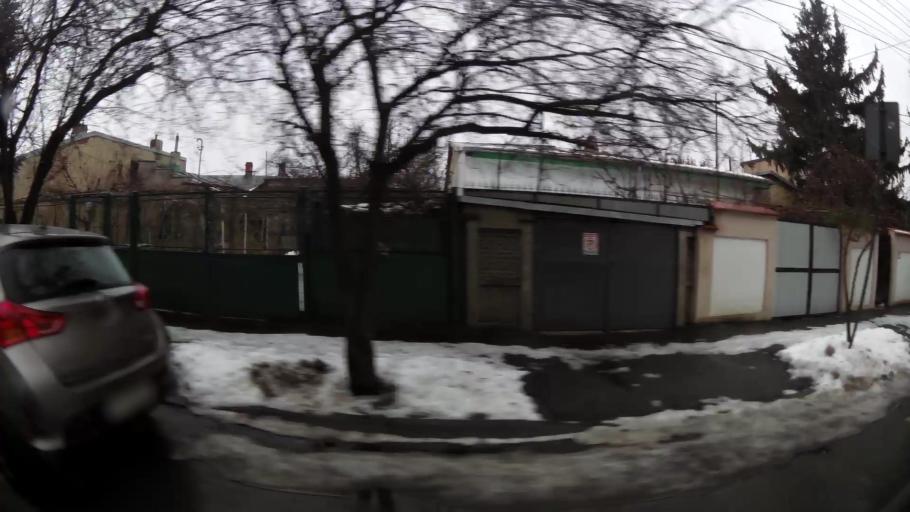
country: RO
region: Ilfov
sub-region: Comuna Chiajna
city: Rosu
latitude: 44.4908
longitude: 26.0438
